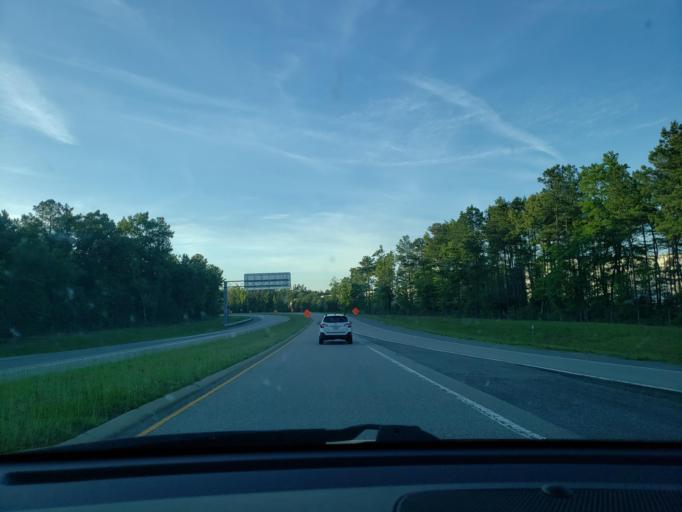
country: US
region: Virginia
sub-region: Henrico County
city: Fort Lee
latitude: 37.4808
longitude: -77.3400
